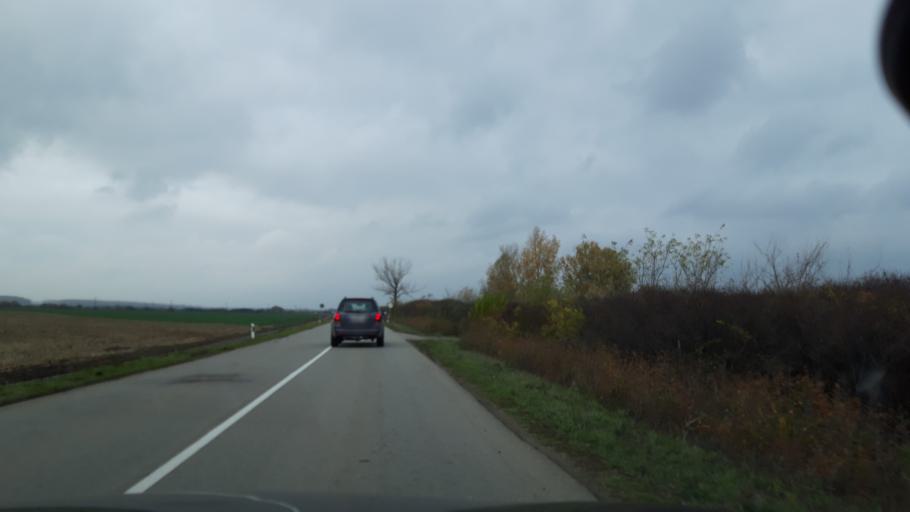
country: RS
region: Autonomna Pokrajina Vojvodina
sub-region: Severnobanatski Okrug
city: Novi Knezevac
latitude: 46.0977
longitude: 20.1093
